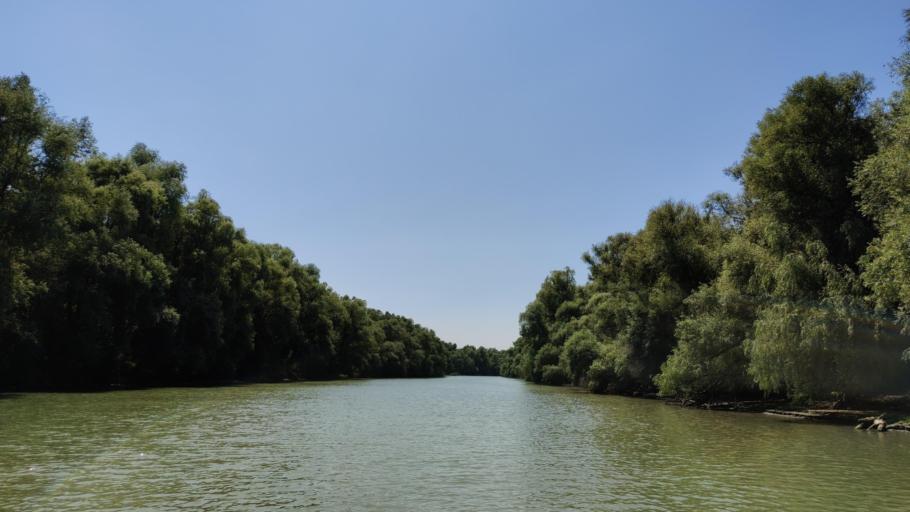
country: RO
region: Tulcea
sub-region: Comuna Pardina
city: Pardina
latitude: 45.2405
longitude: 28.9193
